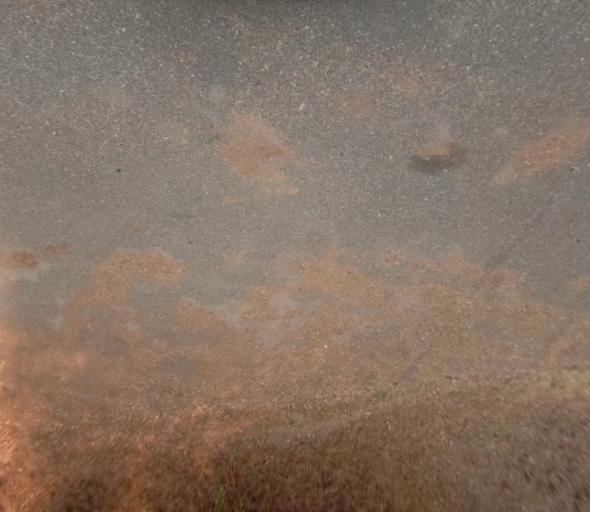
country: US
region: California
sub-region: Madera County
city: Oakhurst
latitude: 37.3174
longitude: -119.6230
